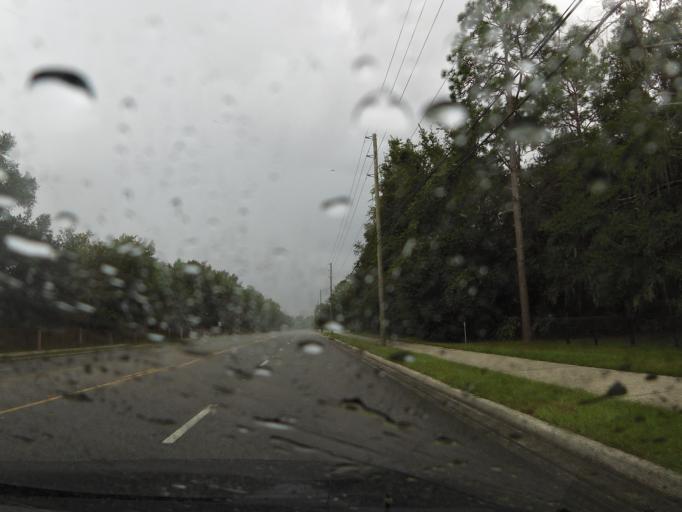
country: US
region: Florida
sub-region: Clay County
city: Asbury Lake
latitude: 30.0370
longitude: -81.8096
